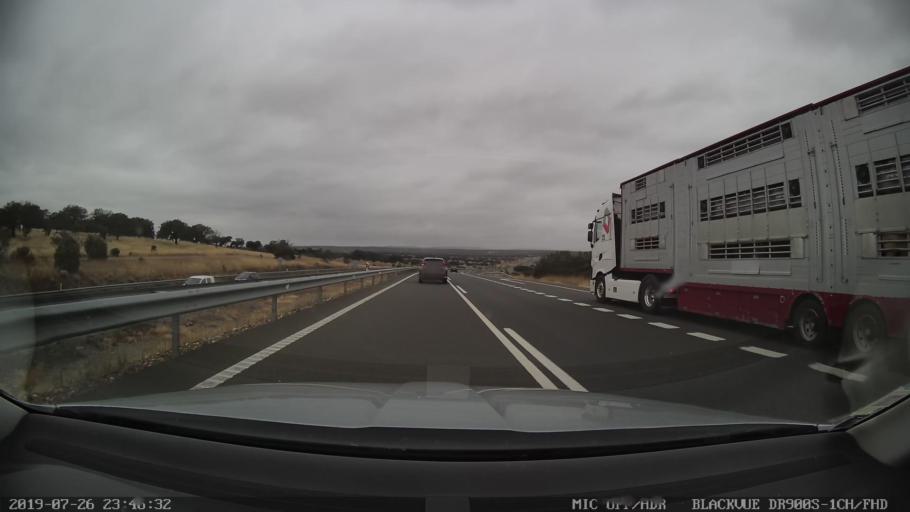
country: ES
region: Extremadura
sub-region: Provincia de Caceres
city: Jaraicejo
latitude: 39.5902
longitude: -5.8365
